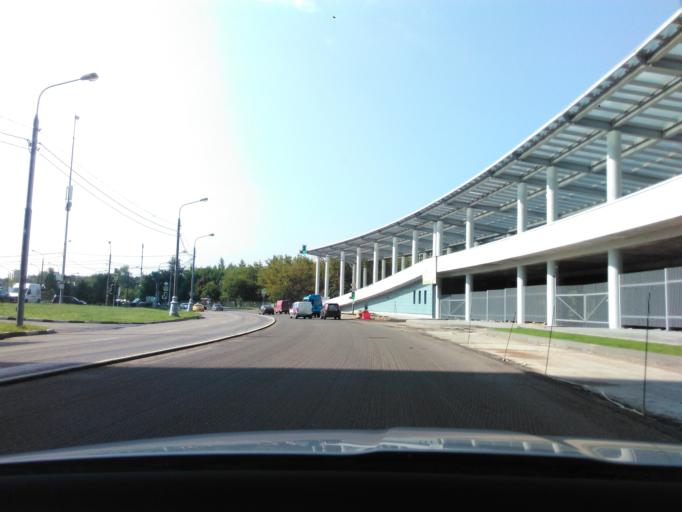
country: RU
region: Moscow
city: Sokol
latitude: 55.7906
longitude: 37.5183
